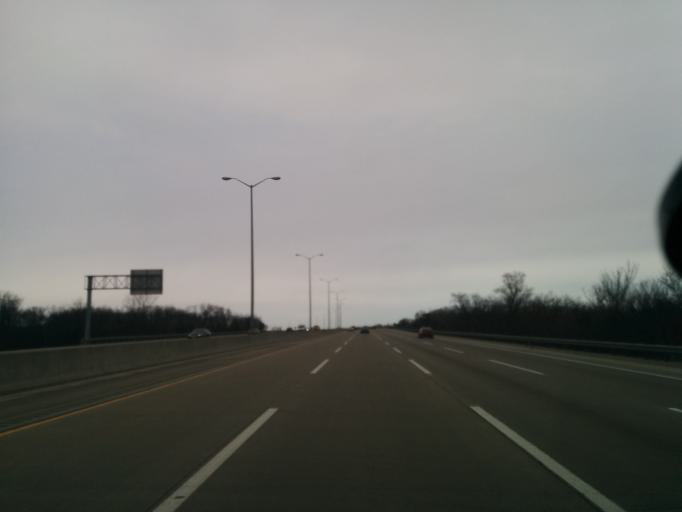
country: US
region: Illinois
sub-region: Cook County
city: Des Plaines
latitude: 42.0796
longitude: -87.8662
